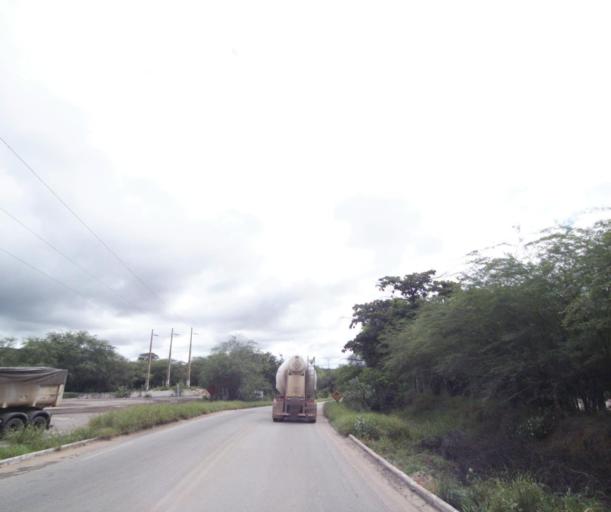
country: BR
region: Bahia
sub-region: Brumado
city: Brumado
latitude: -14.2393
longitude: -41.7226
